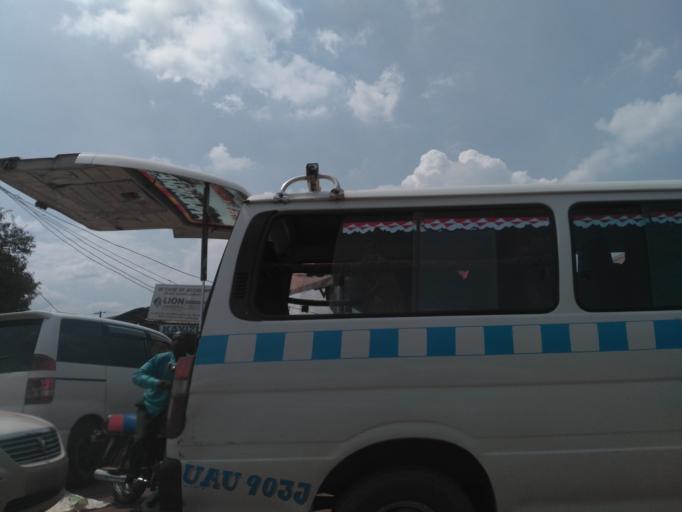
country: UG
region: Central Region
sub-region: Wakiso District
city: Kireka
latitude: 0.4502
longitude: 32.6115
